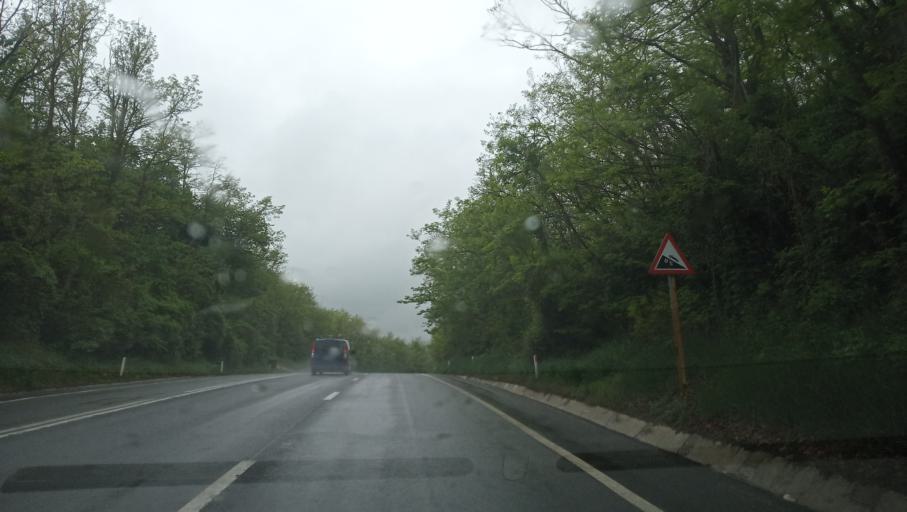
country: RO
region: Sibiu
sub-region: Comuna Orlat
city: Orlat
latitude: 45.7786
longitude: 23.9633
